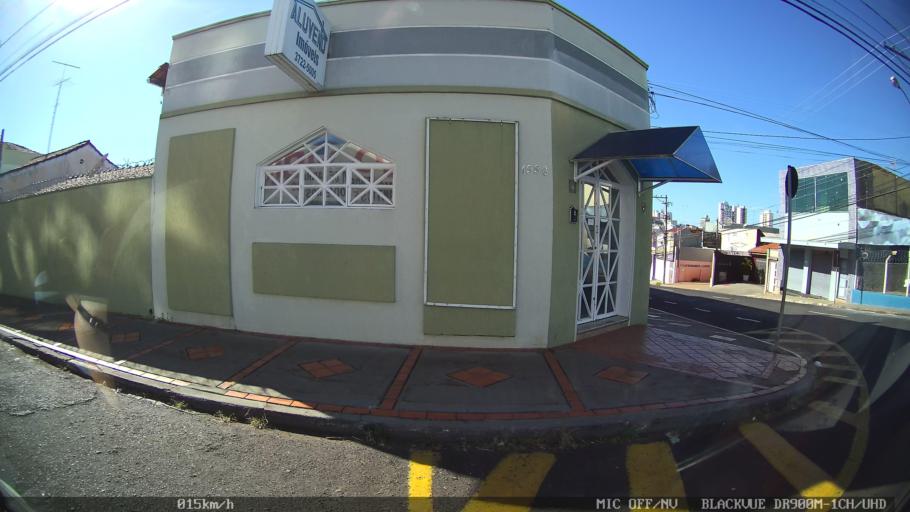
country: BR
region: Sao Paulo
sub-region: Franca
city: Franca
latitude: -20.5347
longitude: -47.4085
